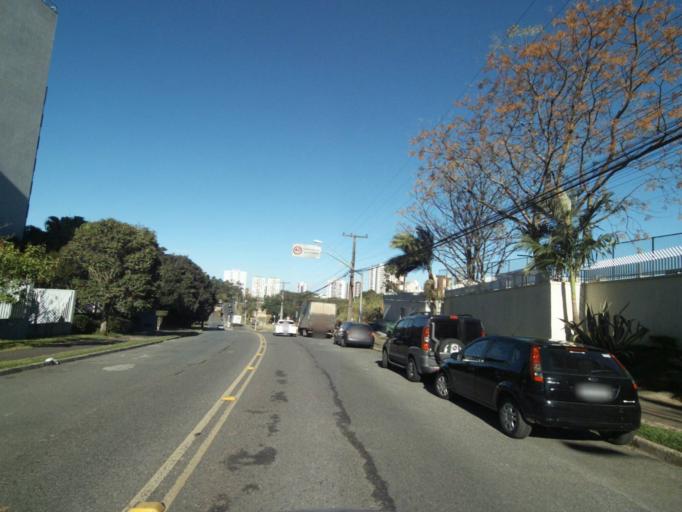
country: BR
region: Parana
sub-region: Curitiba
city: Curitiba
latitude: -25.4013
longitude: -49.2569
